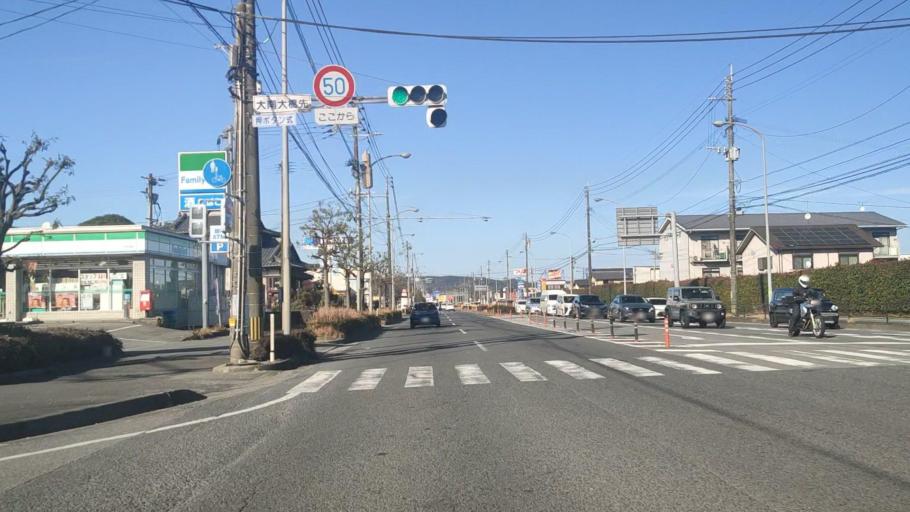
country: JP
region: Oita
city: Oita
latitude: 33.1427
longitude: 131.6580
